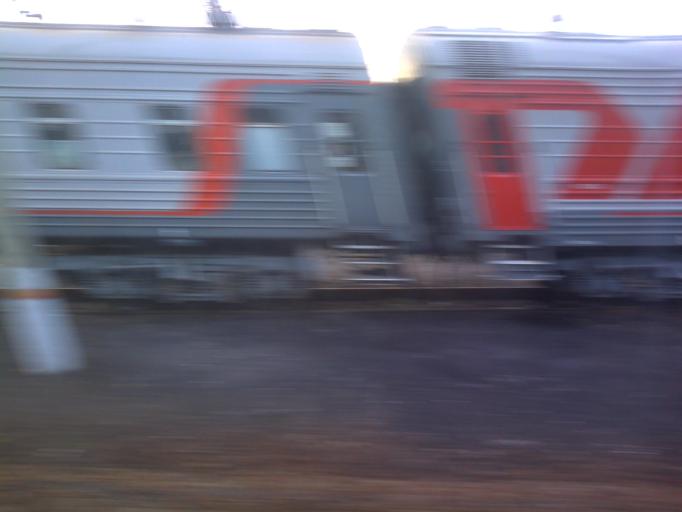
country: RU
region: Moscow
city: Zamoskvorech'ye
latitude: 55.7121
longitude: 37.6386
